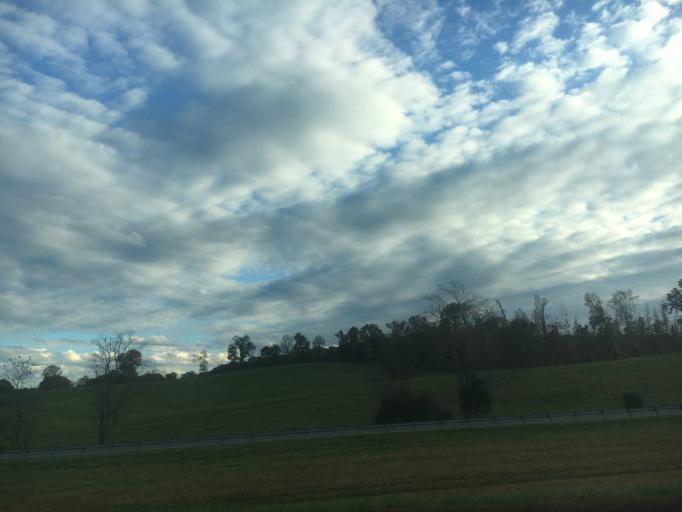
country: US
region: Virginia
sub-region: Washington County
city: Emory
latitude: 36.7524
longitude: -81.8746
